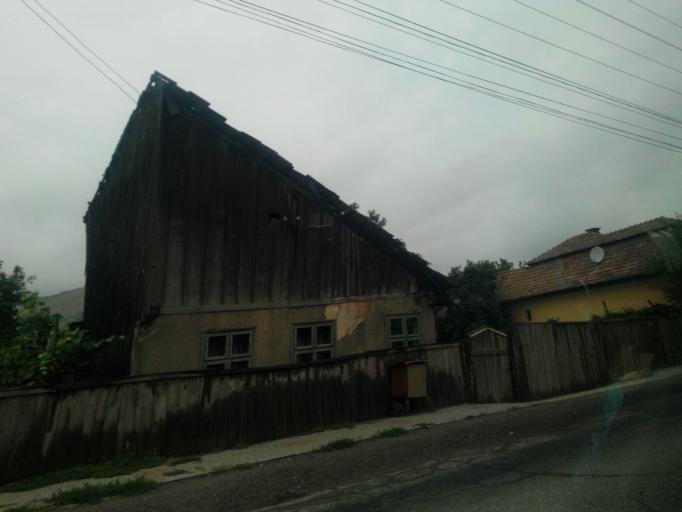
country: RO
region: Cluj
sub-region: Comuna Moldovenesti
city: Moldovenesti
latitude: 46.5251
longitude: 23.6946
